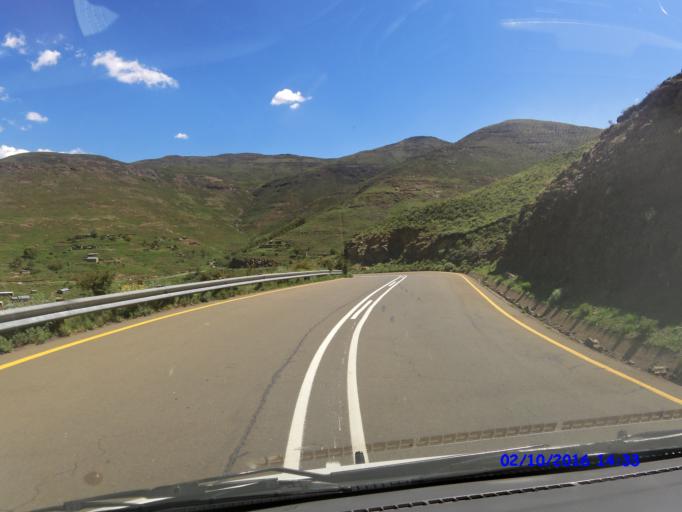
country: LS
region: Maseru
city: Nako
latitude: -29.4883
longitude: 28.0599
